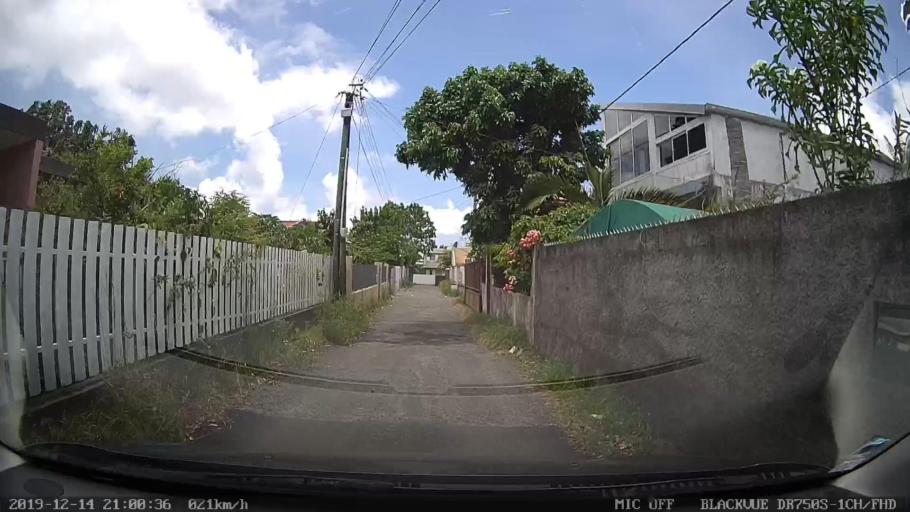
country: RE
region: Reunion
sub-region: Reunion
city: Saint-Andre
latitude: -20.9683
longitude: 55.6589
